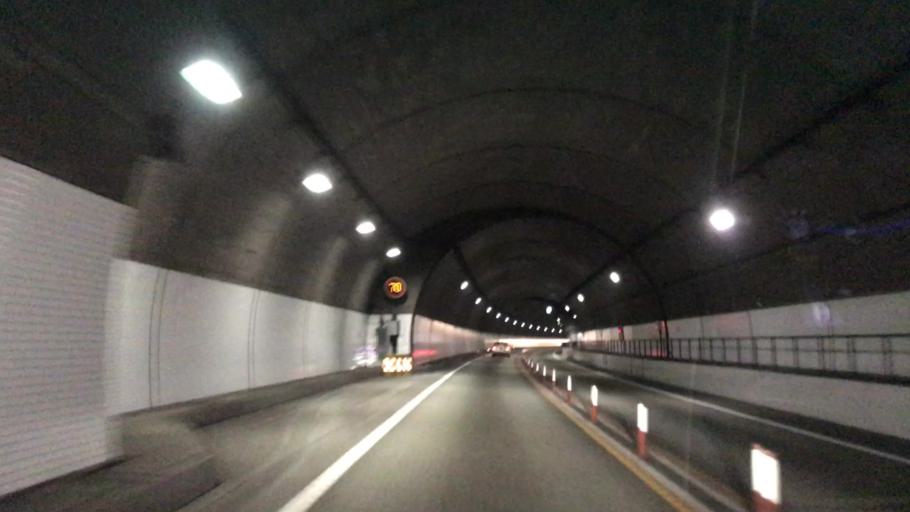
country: JP
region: Hokkaido
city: Iwamizawa
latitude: 42.9346
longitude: 142.0947
